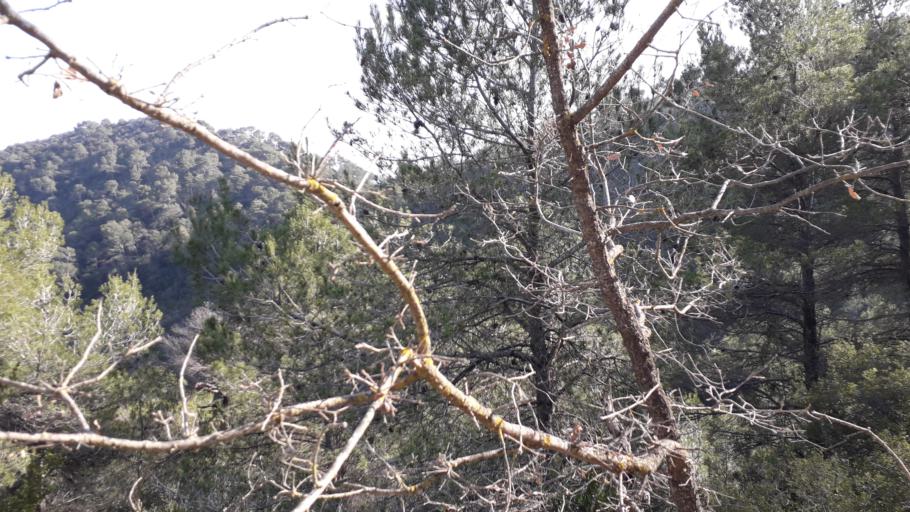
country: ES
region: Catalonia
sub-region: Provincia de Barcelona
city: Sant Marti de Tous
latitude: 41.5194
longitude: 1.4927
